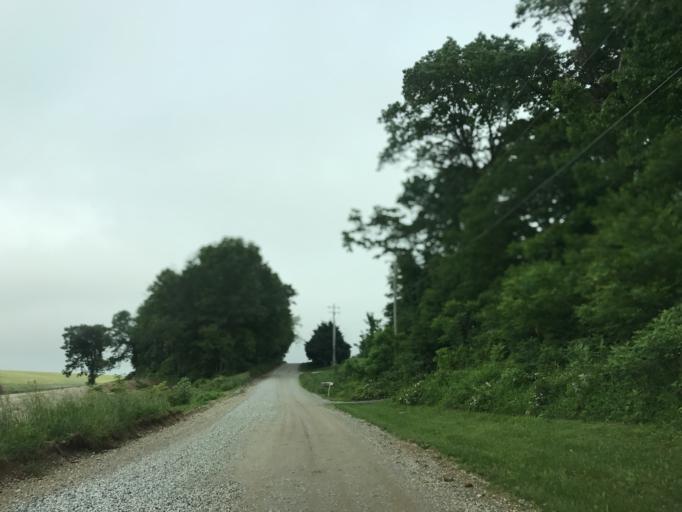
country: US
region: Pennsylvania
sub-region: York County
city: Stewartstown
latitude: 39.7237
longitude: -76.4874
